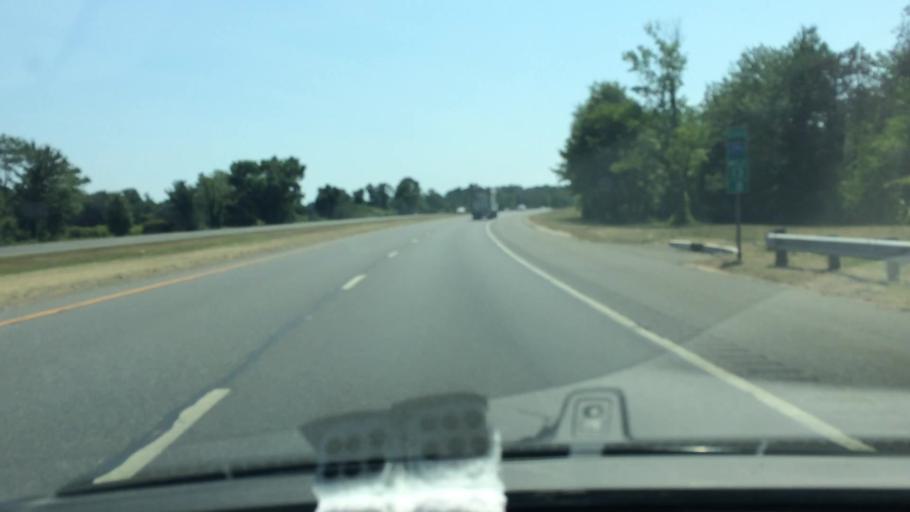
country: US
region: New Jersey
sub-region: Gloucester County
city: Gibbstown
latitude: 39.7986
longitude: -75.3169
